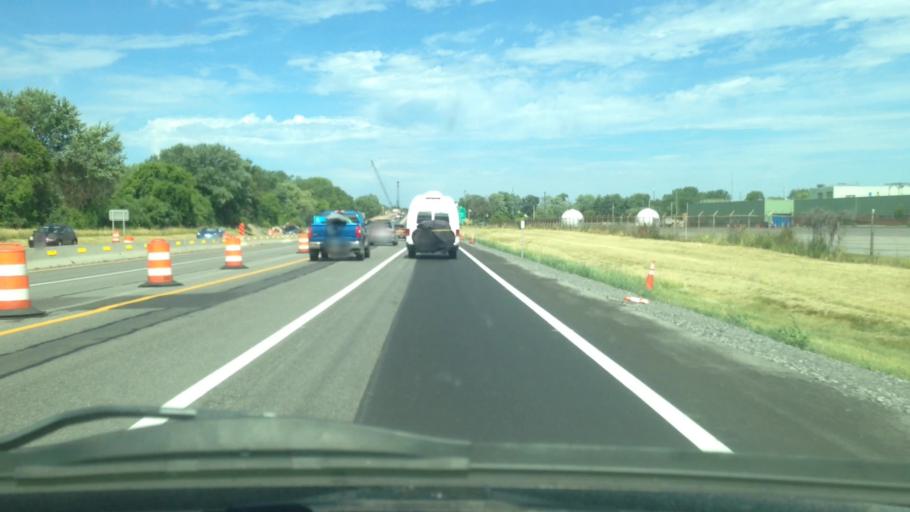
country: US
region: New York
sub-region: Onondaga County
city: Galeville
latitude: 43.1056
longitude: -76.1891
